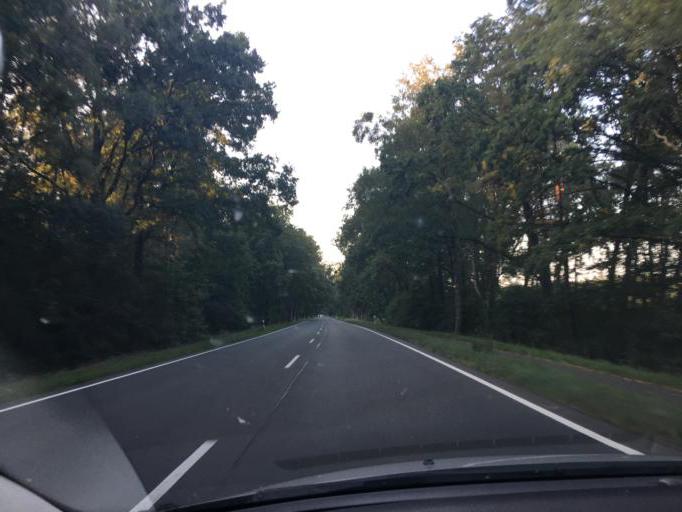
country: DE
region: Lower Saxony
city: Wietzendorf
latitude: 52.9036
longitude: 9.9188
